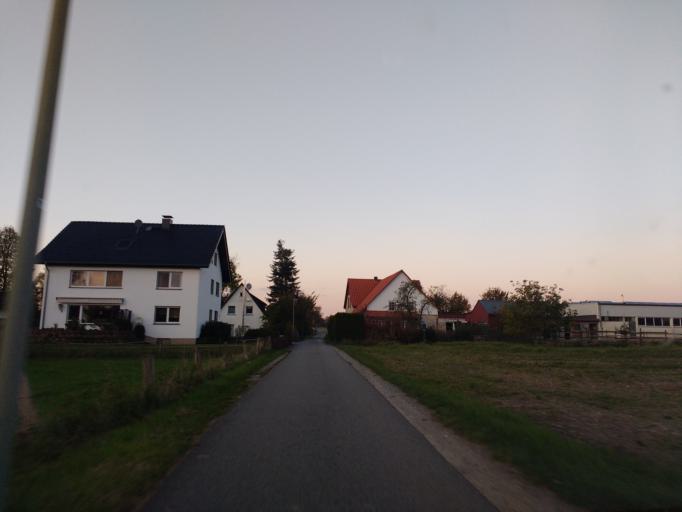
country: DE
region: North Rhine-Westphalia
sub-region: Regierungsbezirk Detmold
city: Schlangen
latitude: 51.7980
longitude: 8.8461
